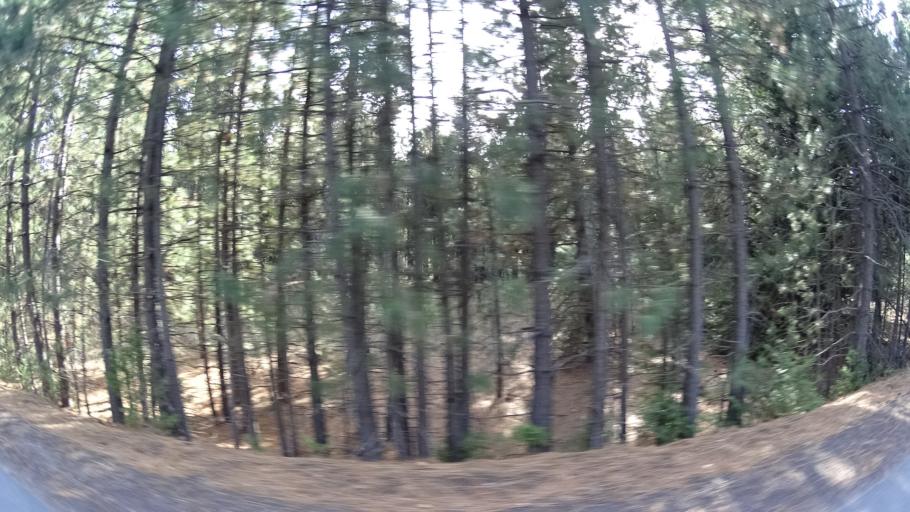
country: US
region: California
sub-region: Siskiyou County
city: Weed
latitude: 41.3832
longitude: -122.3989
